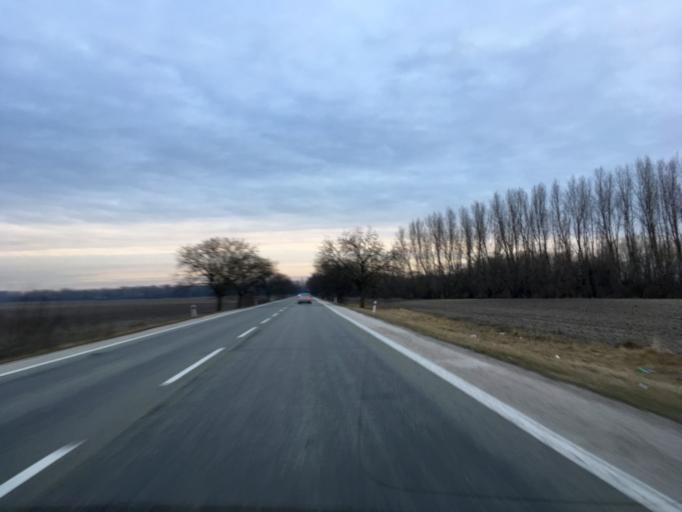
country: SK
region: Trnavsky
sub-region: Okres Dunajska Streda
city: Velky Meder
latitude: 47.9086
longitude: 17.7353
